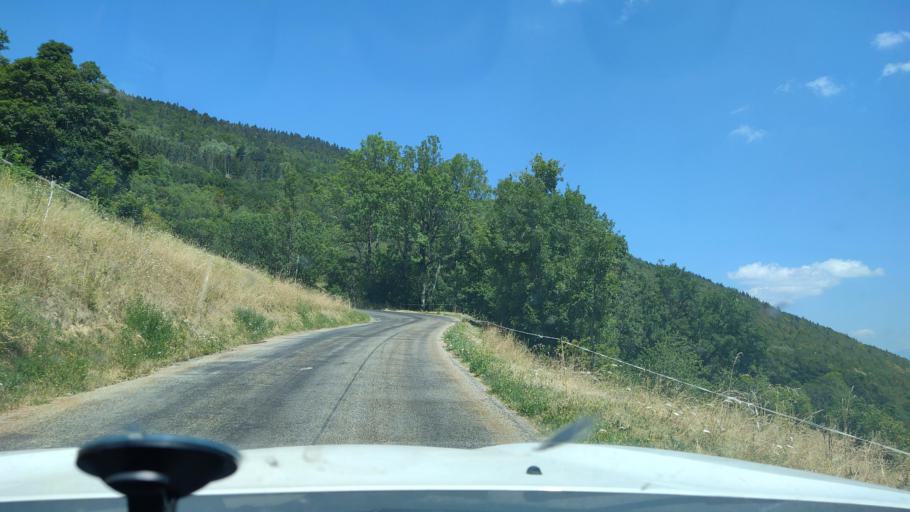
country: FR
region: Rhone-Alpes
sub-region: Departement de la Haute-Savoie
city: Cusy
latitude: 45.6708
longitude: 6.0407
